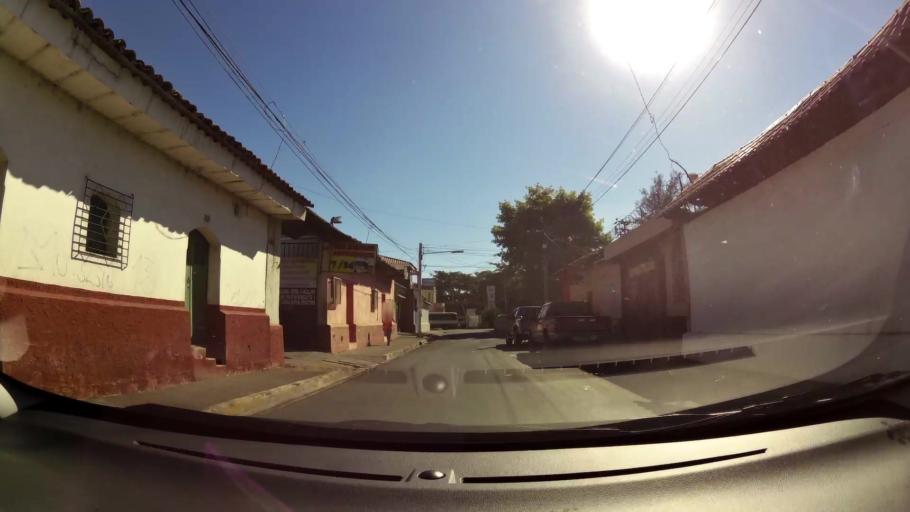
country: SV
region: San Miguel
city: San Miguel
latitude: 13.4731
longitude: -88.1745
